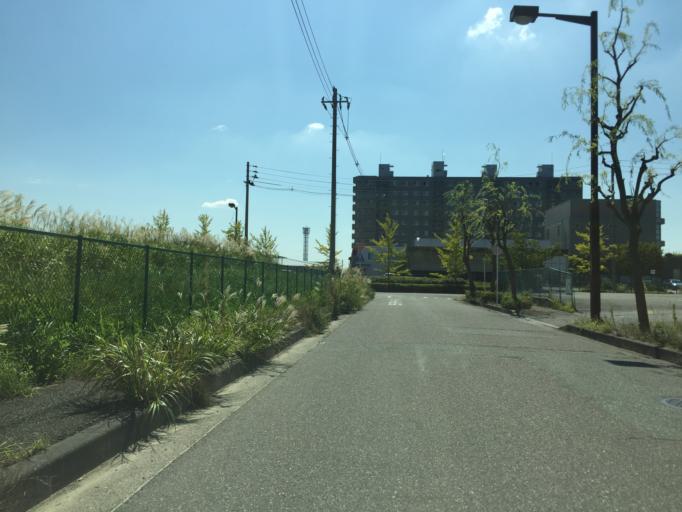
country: JP
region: Niigata
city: Niigata-shi
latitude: 37.8937
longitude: 139.0173
